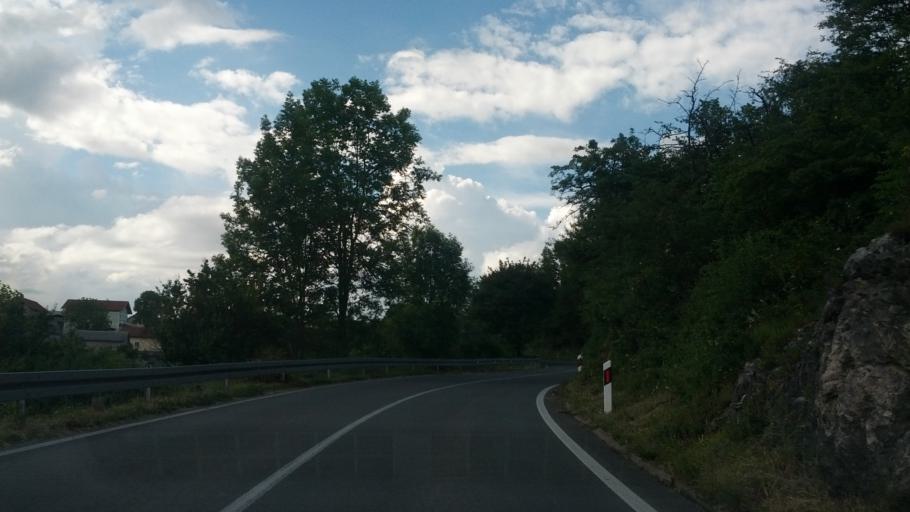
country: BA
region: Federation of Bosnia and Herzegovina
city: Izacic
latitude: 44.8764
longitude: 15.7785
